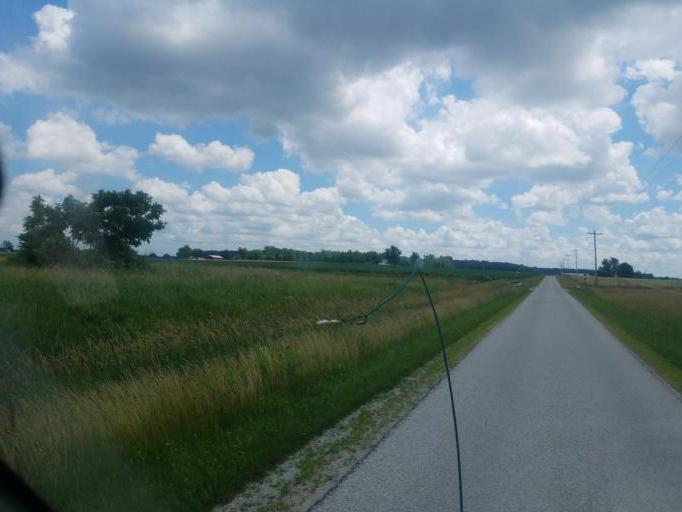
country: US
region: Ohio
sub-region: Huron County
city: Willard
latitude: 41.0013
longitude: -82.8297
